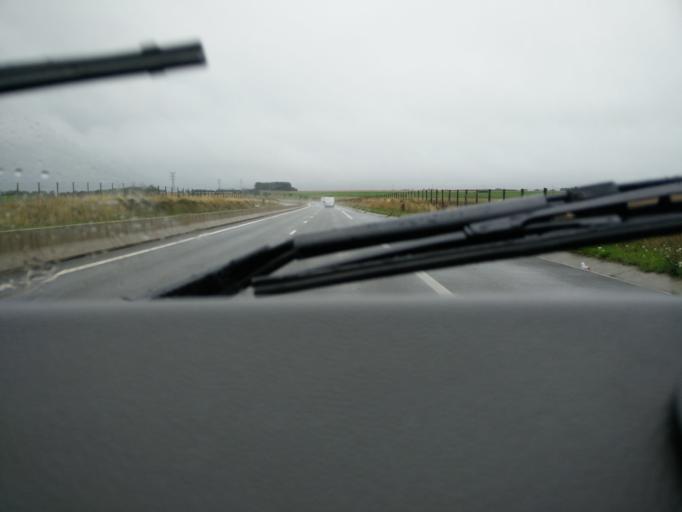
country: FR
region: Nord-Pas-de-Calais
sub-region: Departement du Pas-de-Calais
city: Marconnelle
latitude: 50.3638
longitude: 1.9691
